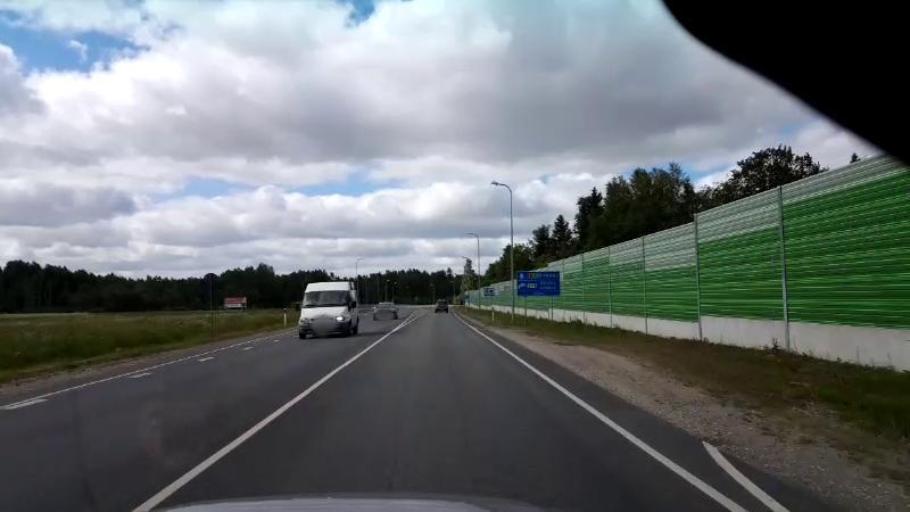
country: EE
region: Paernumaa
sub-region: Sauga vald
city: Sauga
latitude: 58.4260
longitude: 24.4957
